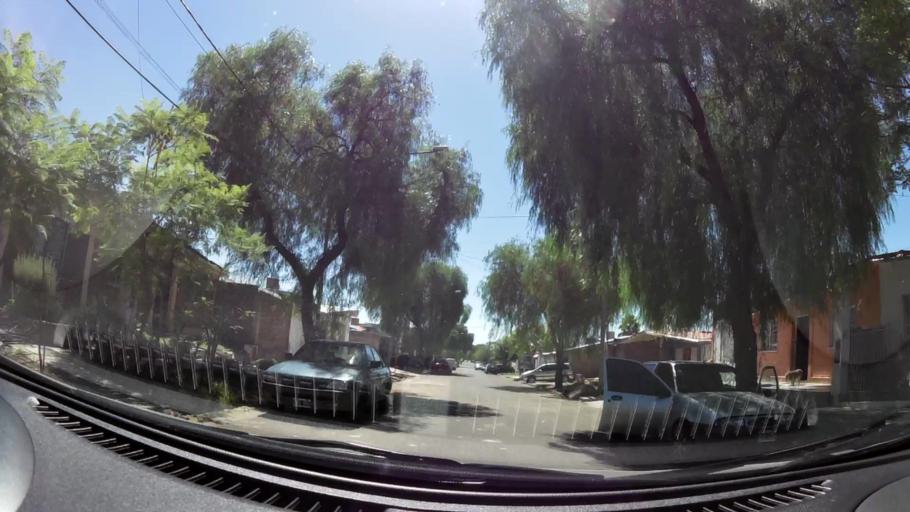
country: AR
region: Mendoza
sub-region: Departamento de Godoy Cruz
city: Godoy Cruz
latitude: -32.9472
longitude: -68.8688
